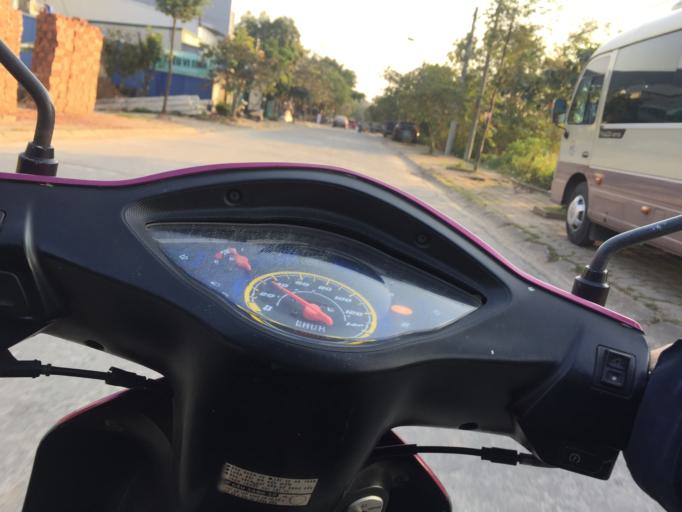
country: VN
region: Ha Noi
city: Chuc Son
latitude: 20.9181
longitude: 105.7144
